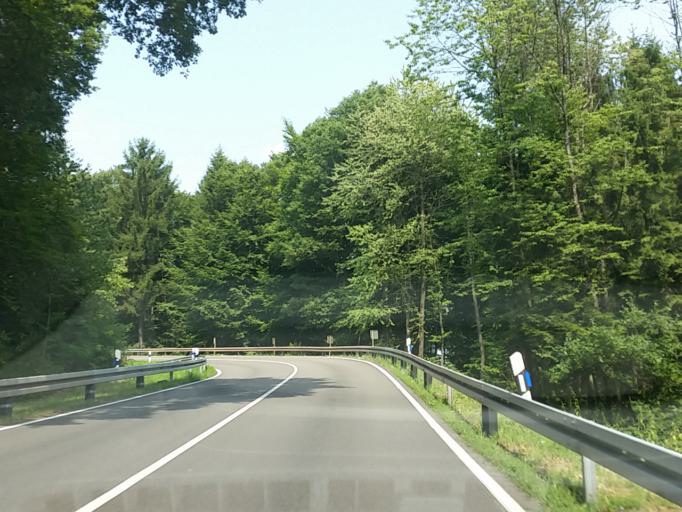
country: DE
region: Saarland
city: Lebach
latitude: 49.4208
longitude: 6.8908
